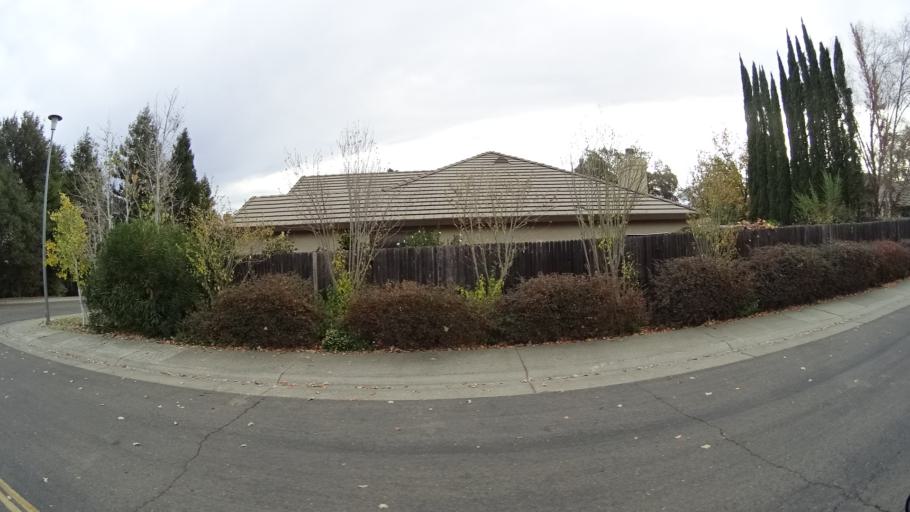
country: US
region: California
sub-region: Sacramento County
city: Citrus Heights
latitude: 38.7181
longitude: -121.2457
